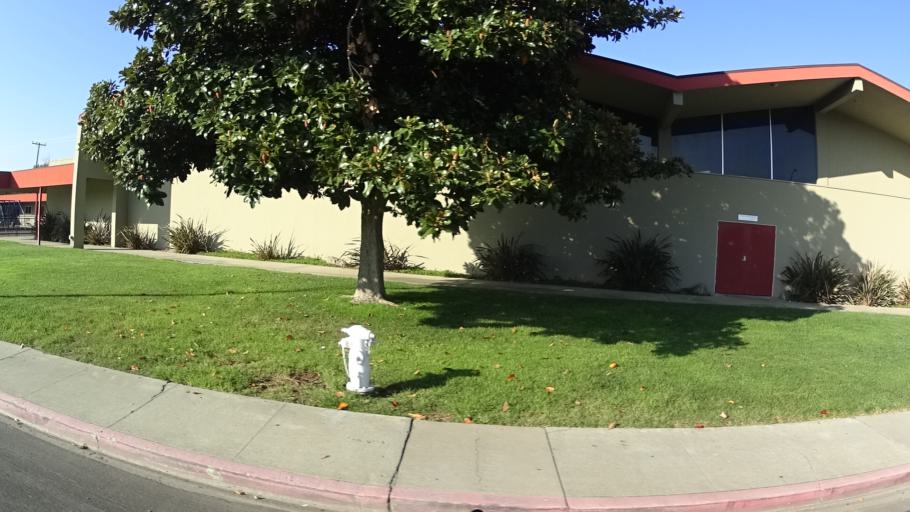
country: US
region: California
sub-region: Santa Clara County
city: Santa Clara
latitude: 37.3466
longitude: -121.9833
